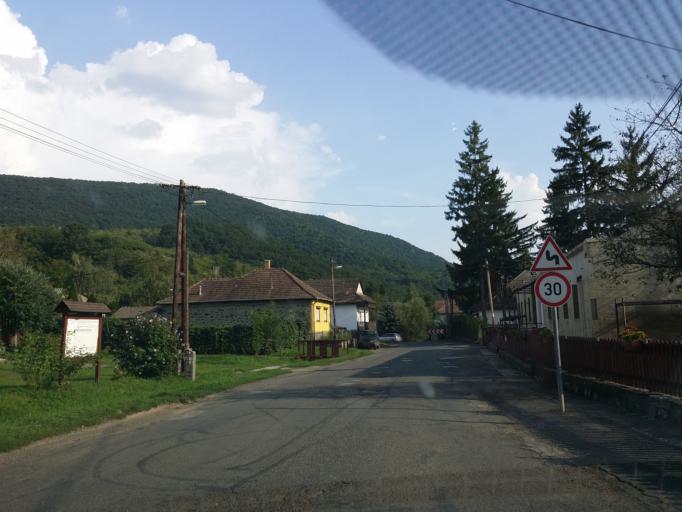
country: HU
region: Nograd
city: Bujak
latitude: 47.9392
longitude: 19.5835
